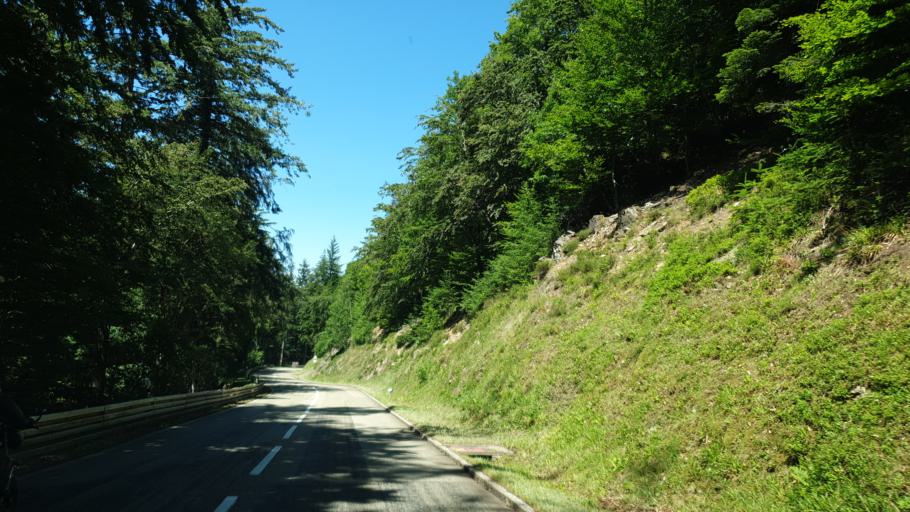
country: DE
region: Baden-Wuerttemberg
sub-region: Freiburg Region
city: Horben
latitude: 47.9238
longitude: 7.8738
